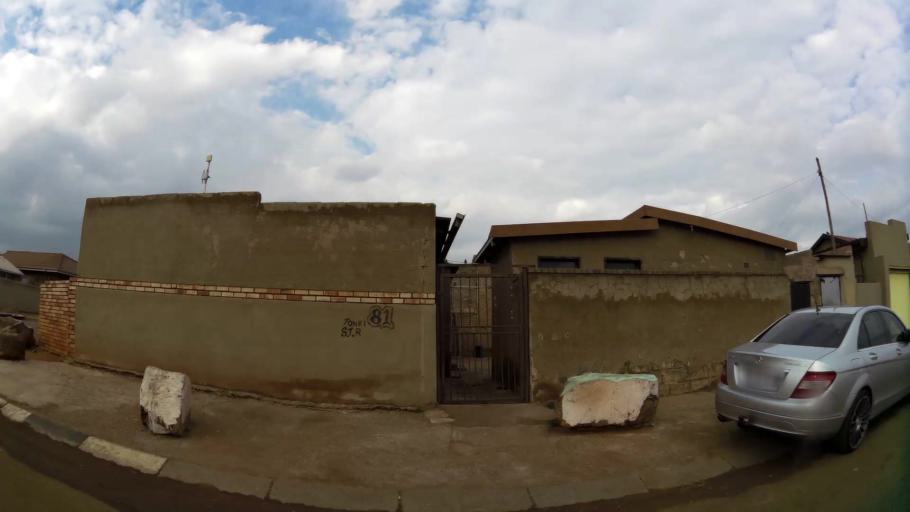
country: ZA
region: Gauteng
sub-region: City of Johannesburg Metropolitan Municipality
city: Soweto
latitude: -26.2458
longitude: 27.8122
